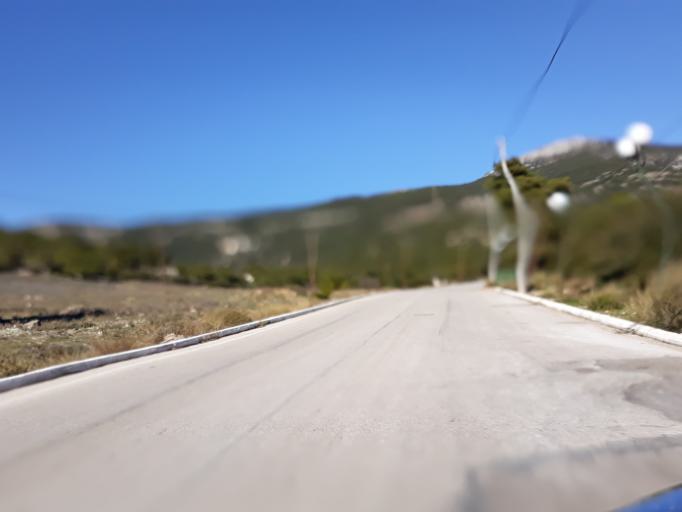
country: GR
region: Attica
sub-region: Nomarchia Dytikis Attikis
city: Fyli
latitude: 38.0997
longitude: 23.6816
